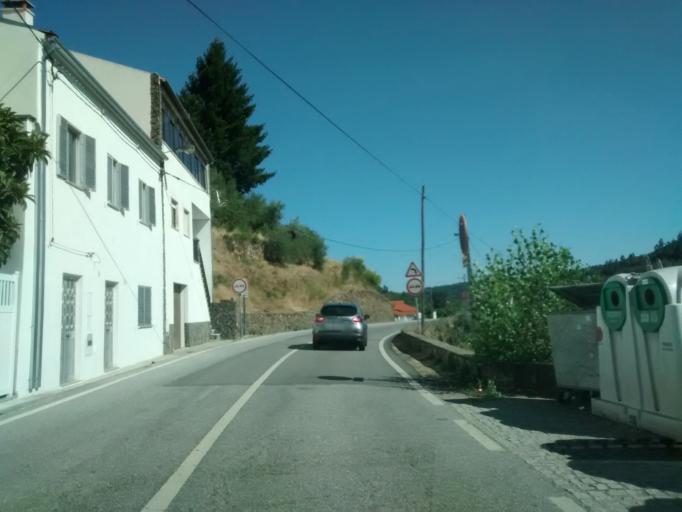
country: PT
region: Castelo Branco
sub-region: Belmonte
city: Belmonte
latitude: 40.4063
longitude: -7.4013
